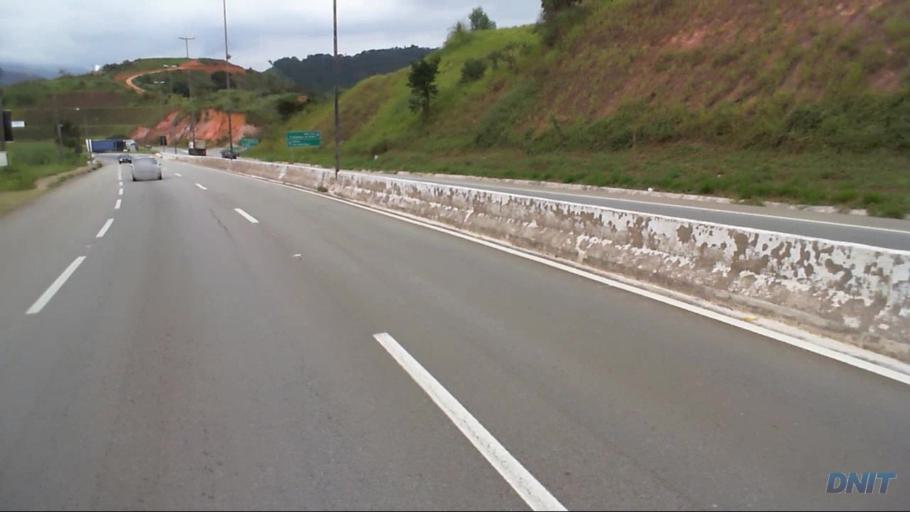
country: BR
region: Minas Gerais
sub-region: Nova Era
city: Nova Era
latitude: -19.7586
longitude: -43.0285
